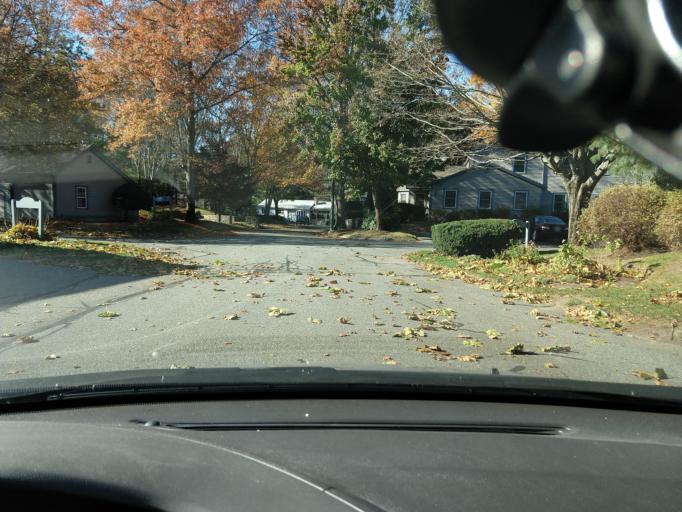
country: US
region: Massachusetts
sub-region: Middlesex County
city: Bedford
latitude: 42.4892
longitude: -71.2563
